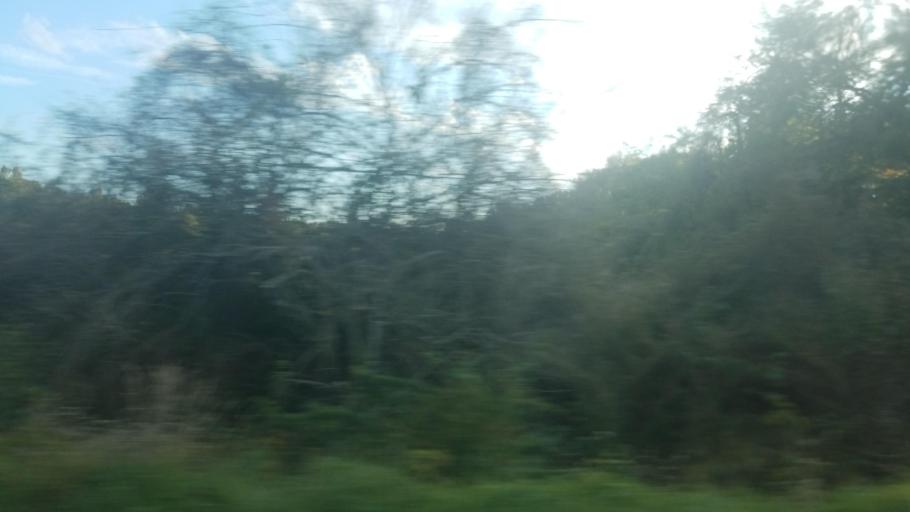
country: US
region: Illinois
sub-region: Saline County
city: Carrier Mills
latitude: 37.8051
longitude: -88.6882
